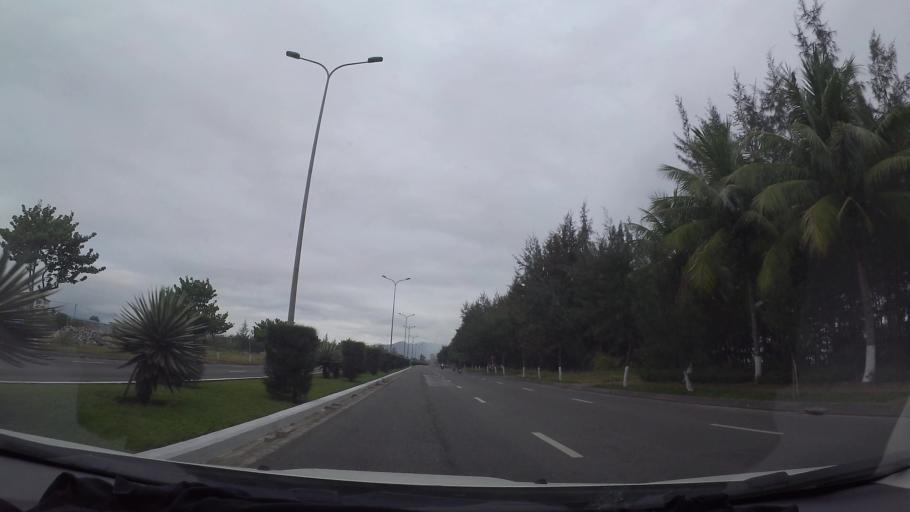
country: VN
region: Da Nang
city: Lien Chieu
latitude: 16.0930
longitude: 108.1486
